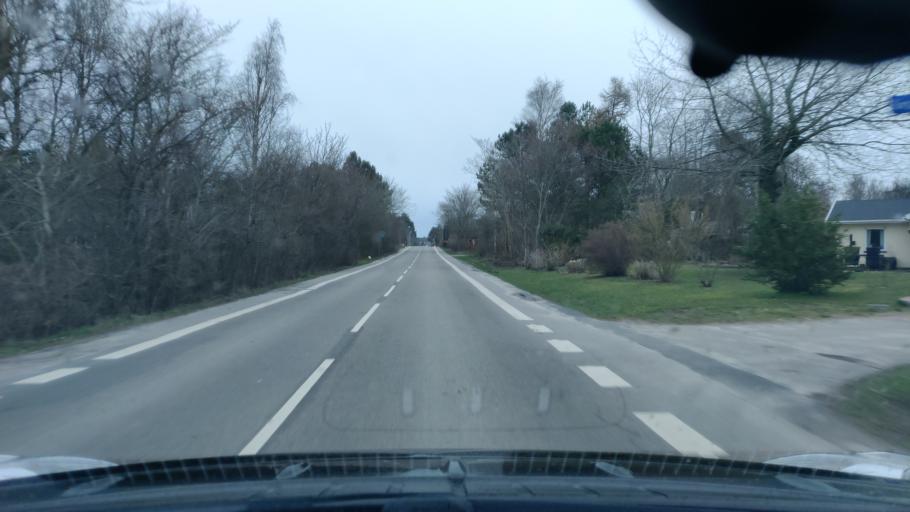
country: DK
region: Zealand
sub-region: Odsherred Kommune
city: Asnaes
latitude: 55.8627
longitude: 11.5315
